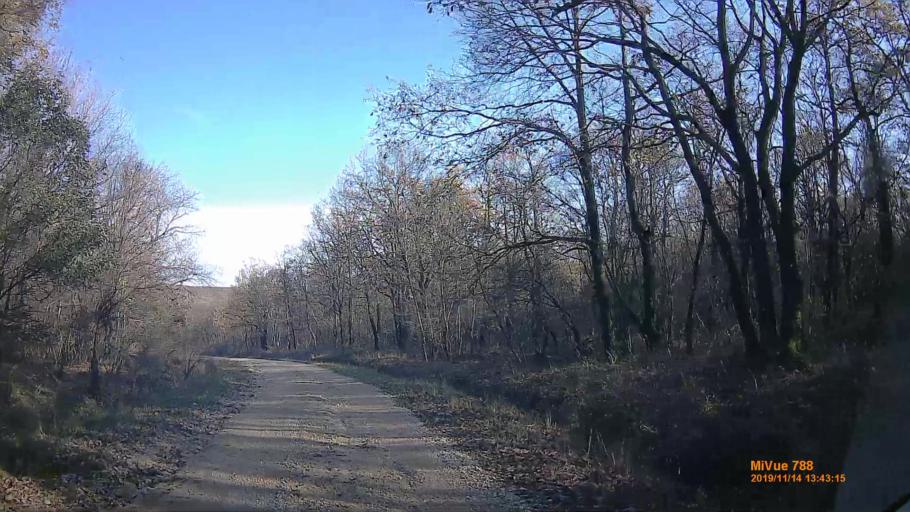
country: HU
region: Veszprem
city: Veszprem
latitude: 47.1822
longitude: 17.9252
